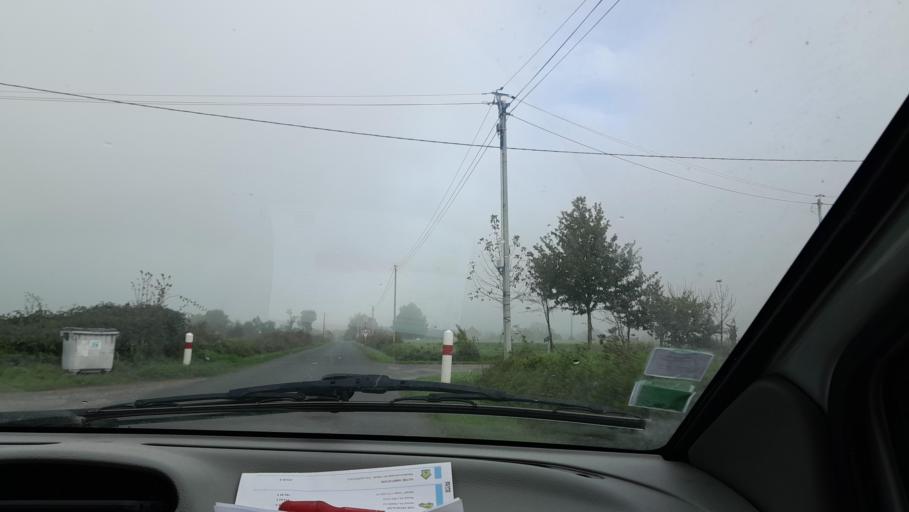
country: FR
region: Pays de la Loire
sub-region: Departement de la Mayenne
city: Saint-Pierre-la-Cour
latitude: 48.1406
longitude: -1.0278
